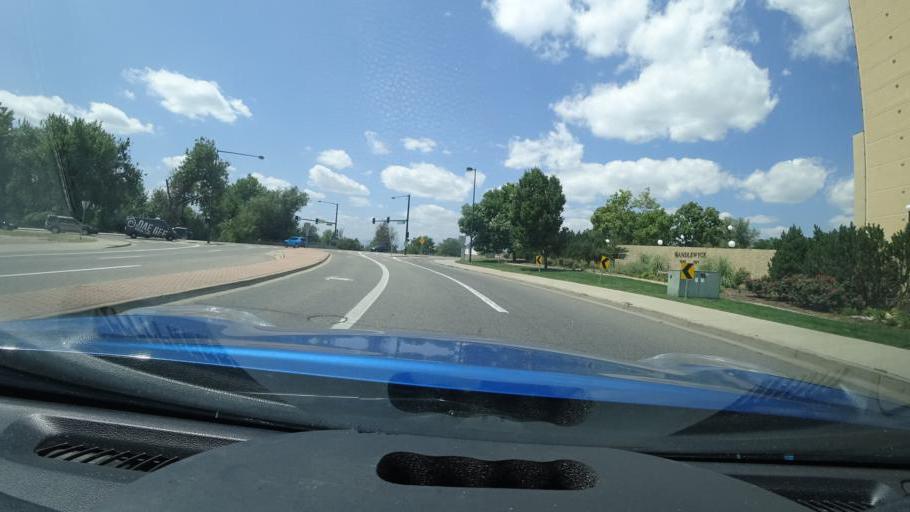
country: US
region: Colorado
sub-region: Arapahoe County
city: Glendale
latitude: 39.6965
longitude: -104.8967
